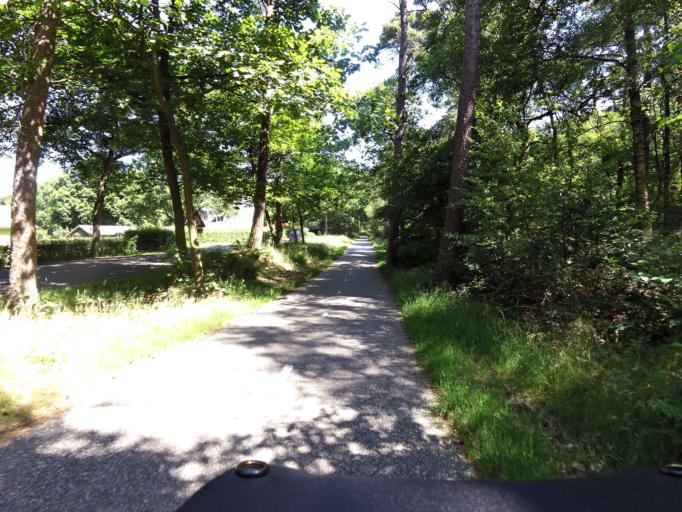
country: NL
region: Overijssel
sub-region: Gemeente Twenterand
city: Magele
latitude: 52.5097
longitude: 6.5150
